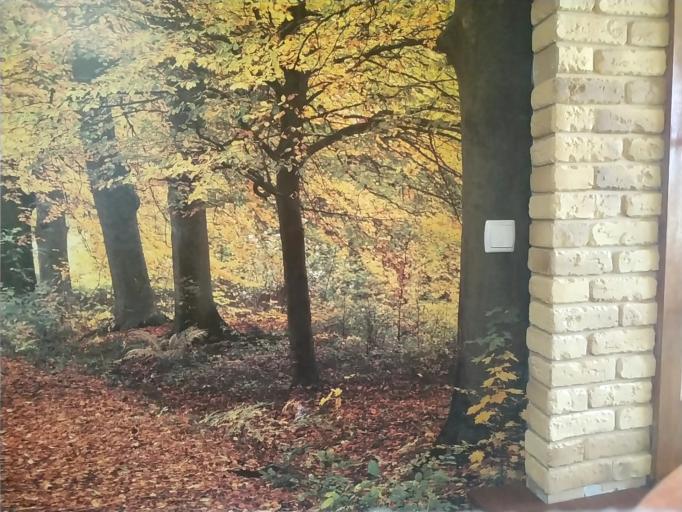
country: RU
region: Tverskaya
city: Vyshniy Volochek
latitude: 57.6428
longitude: 34.5605
